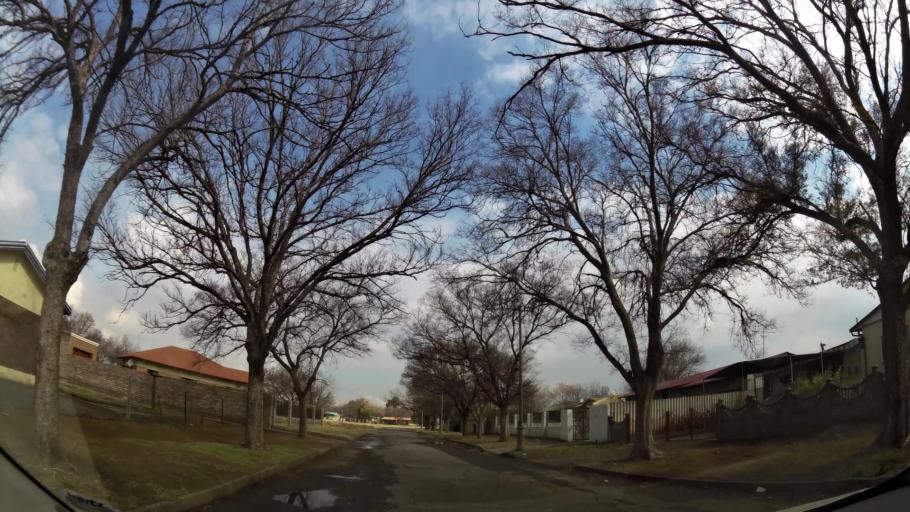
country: ZA
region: Gauteng
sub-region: Sedibeng District Municipality
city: Vereeniging
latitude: -26.6642
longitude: 27.9189
